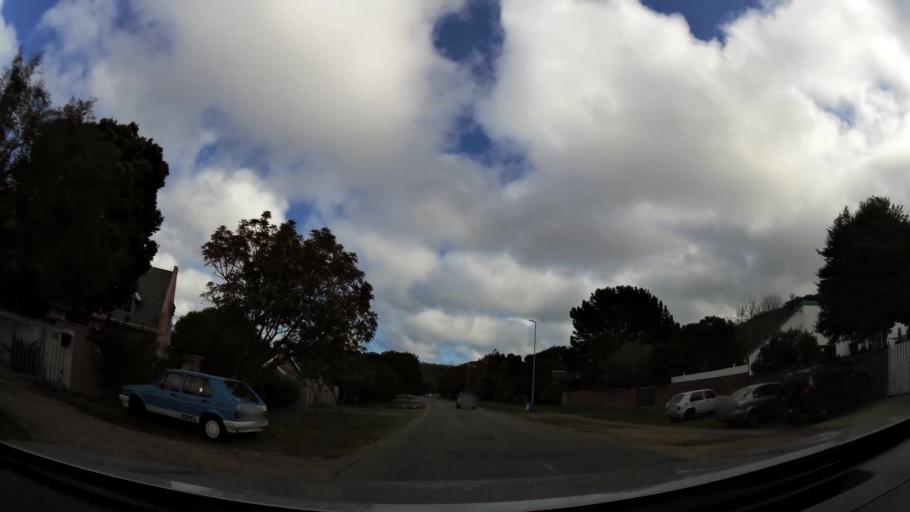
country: ZA
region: Western Cape
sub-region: Eden District Municipality
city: Plettenberg Bay
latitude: -34.0777
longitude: 23.3647
